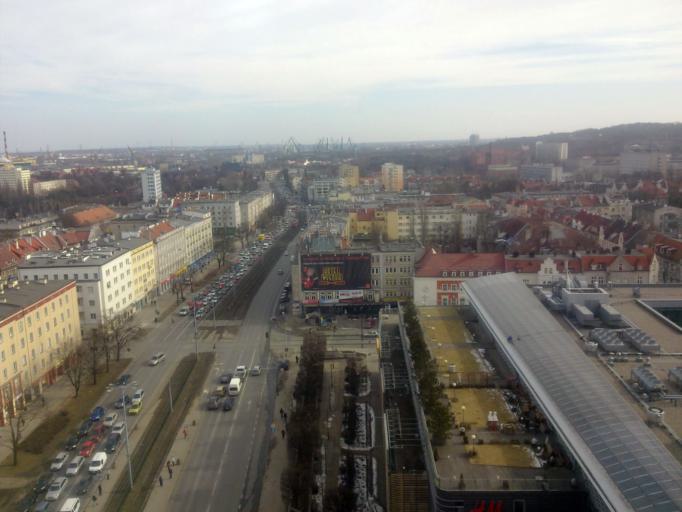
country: PL
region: Pomeranian Voivodeship
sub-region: Gdansk
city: Gdansk
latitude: 54.3763
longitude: 18.6087
